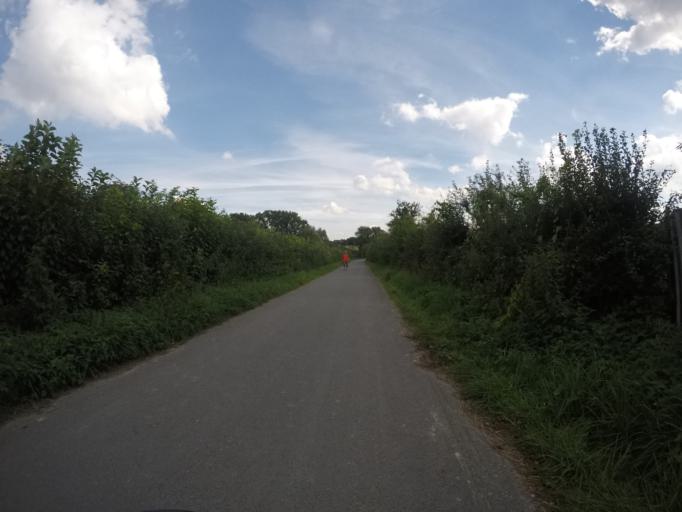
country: DE
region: North Rhine-Westphalia
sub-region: Regierungsbezirk Detmold
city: Bielefeld
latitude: 52.0581
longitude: 8.5877
